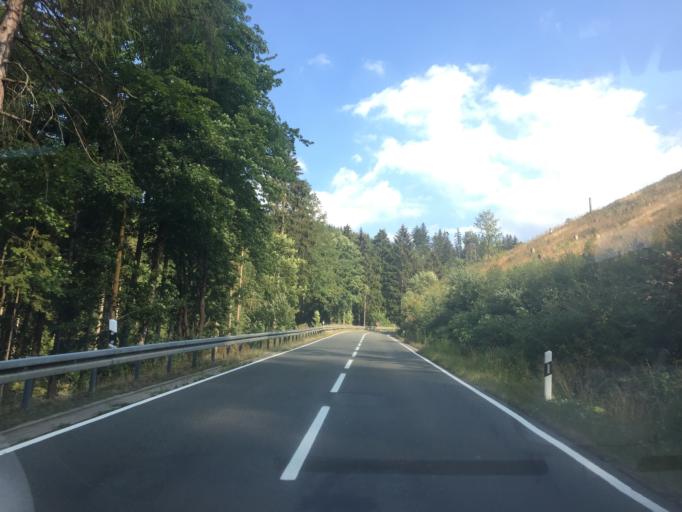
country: DE
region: Saxony-Anhalt
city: Darlingerode
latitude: 51.7897
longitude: 10.7387
